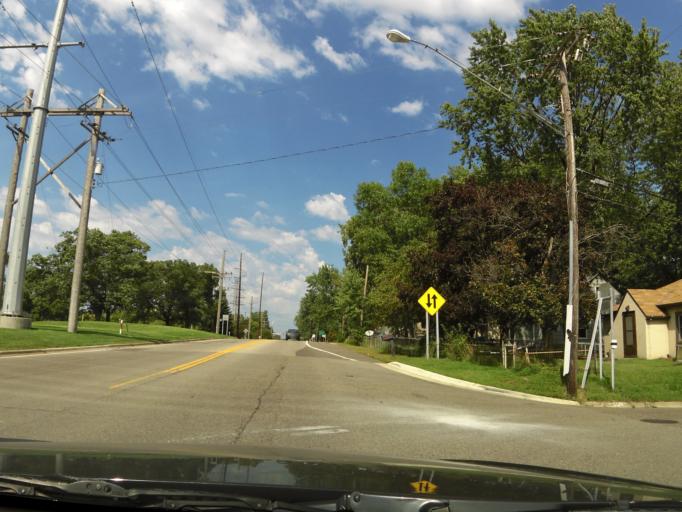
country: US
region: Minnesota
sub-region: Ramsey County
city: Maplewood
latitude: 44.9536
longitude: -92.9847
